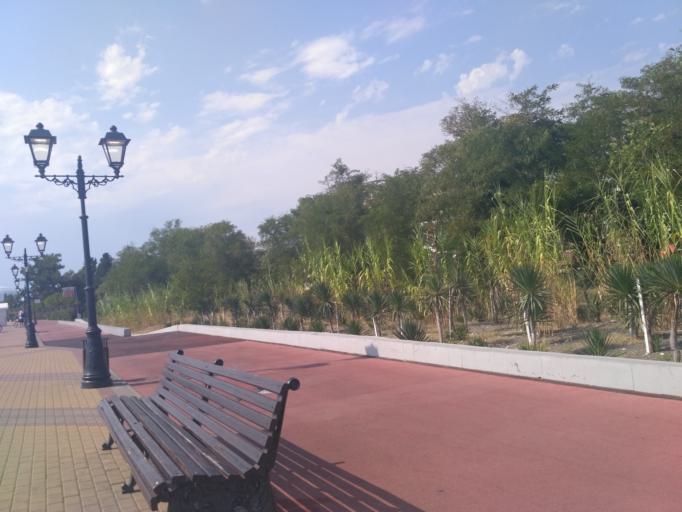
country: RU
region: Krasnodarskiy
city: Adler
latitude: 43.3957
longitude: 39.9715
